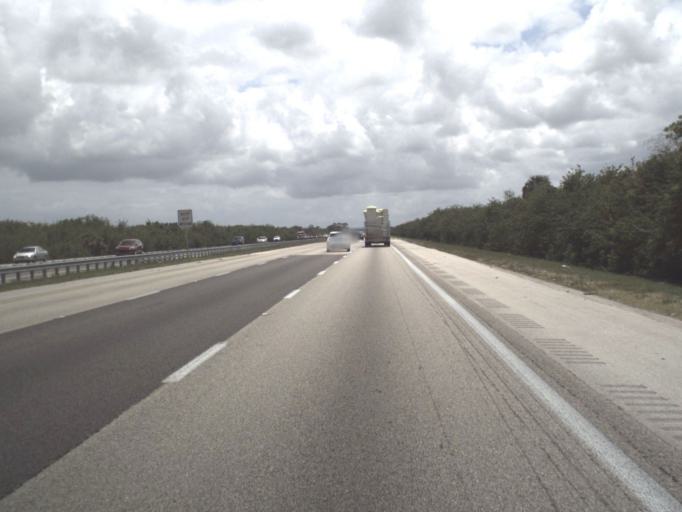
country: US
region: Florida
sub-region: Brevard County
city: Rockledge
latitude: 28.2792
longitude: -80.7328
